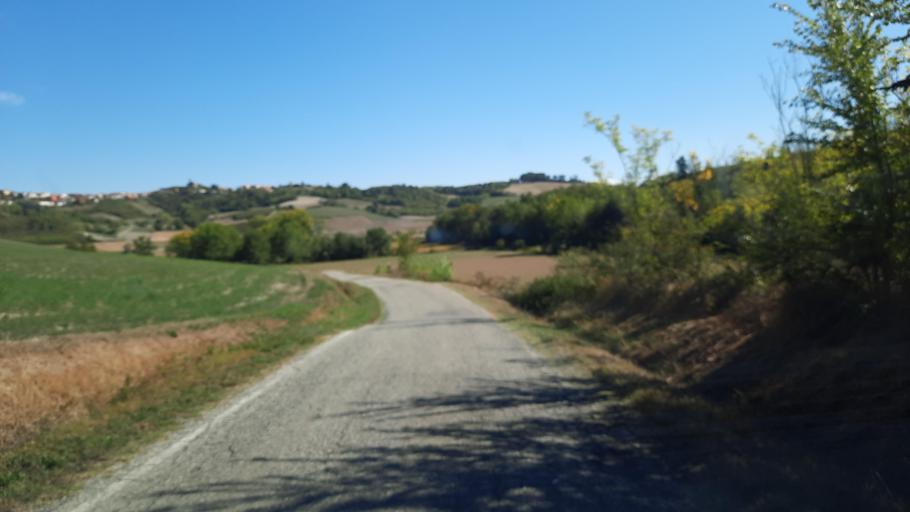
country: IT
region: Piedmont
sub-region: Provincia di Alessandria
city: Camagna Monferrato
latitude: 45.0023
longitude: 8.4376
